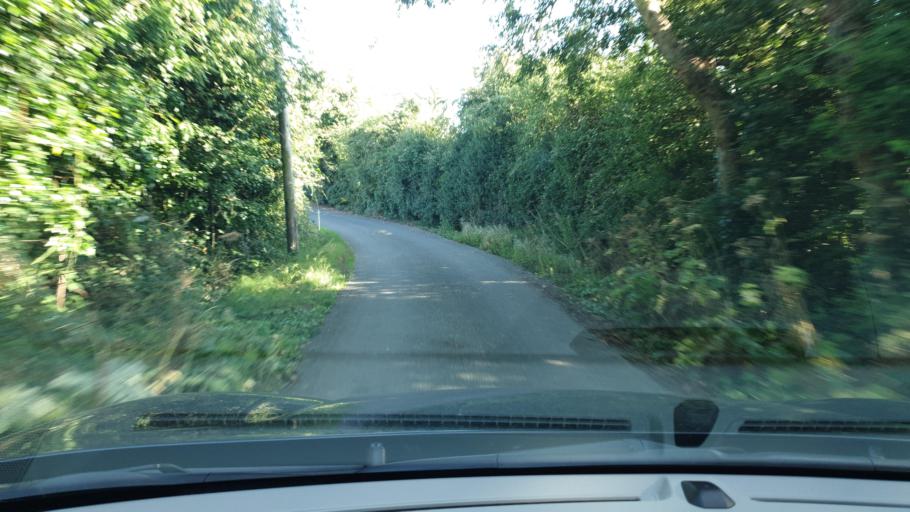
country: IE
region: Leinster
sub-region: An Mhi
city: Stamullin
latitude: 53.5900
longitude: -6.2578
